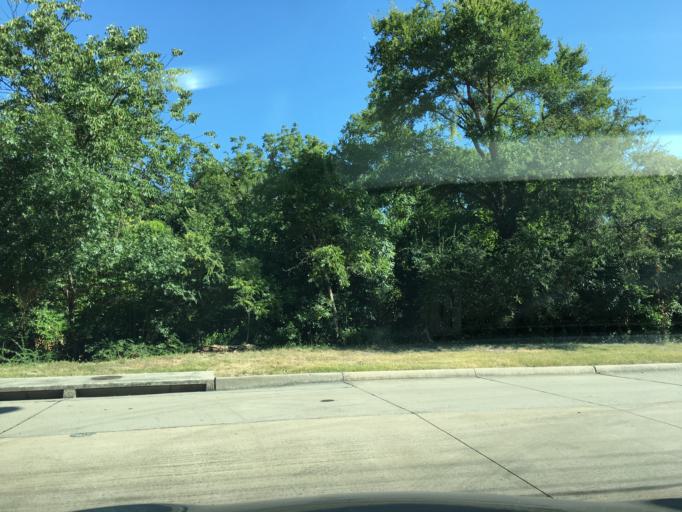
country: US
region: Texas
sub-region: Dallas County
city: Garland
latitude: 32.8542
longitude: -96.6956
